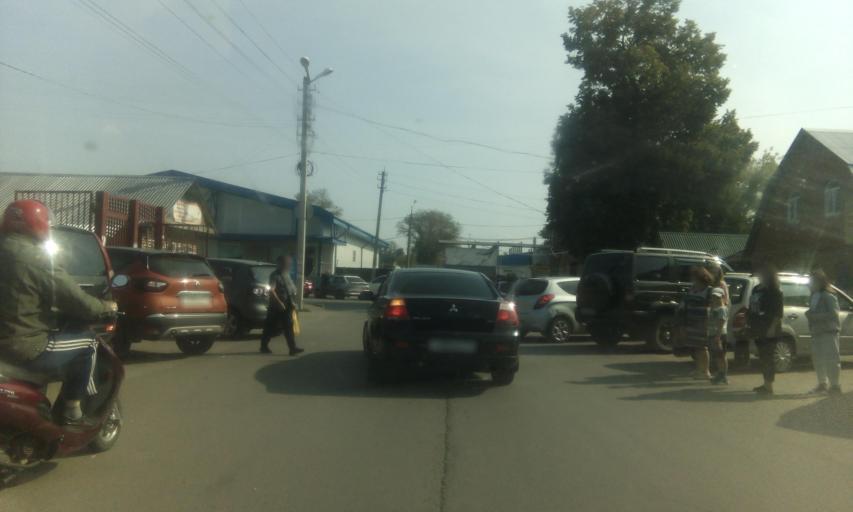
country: RU
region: Tula
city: Uzlovaya
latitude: 53.9743
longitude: 38.1669
